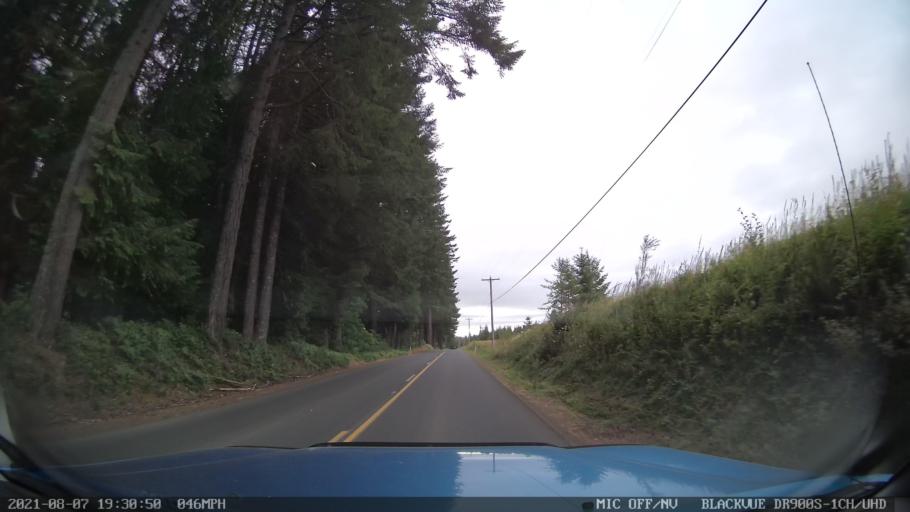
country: US
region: Oregon
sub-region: Linn County
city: Lyons
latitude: 44.8877
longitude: -122.6260
